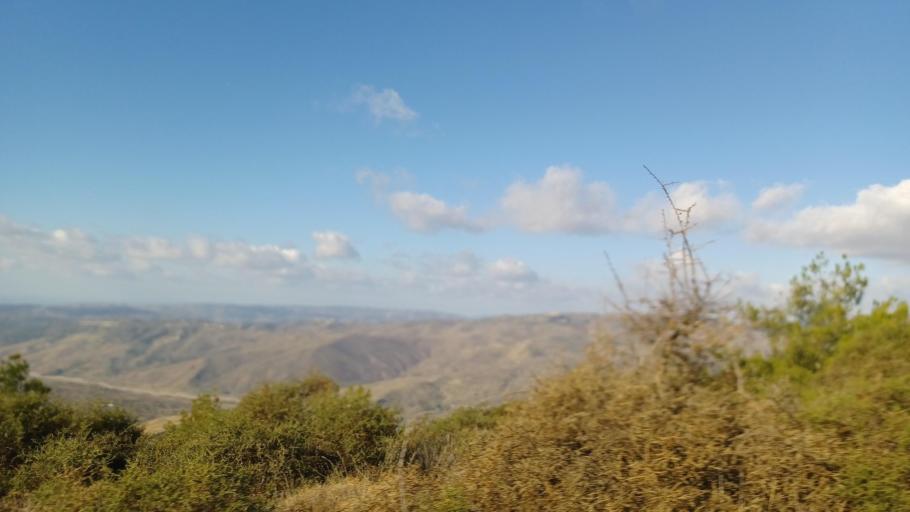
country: CY
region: Limassol
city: Pachna
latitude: 34.8407
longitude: 32.6811
